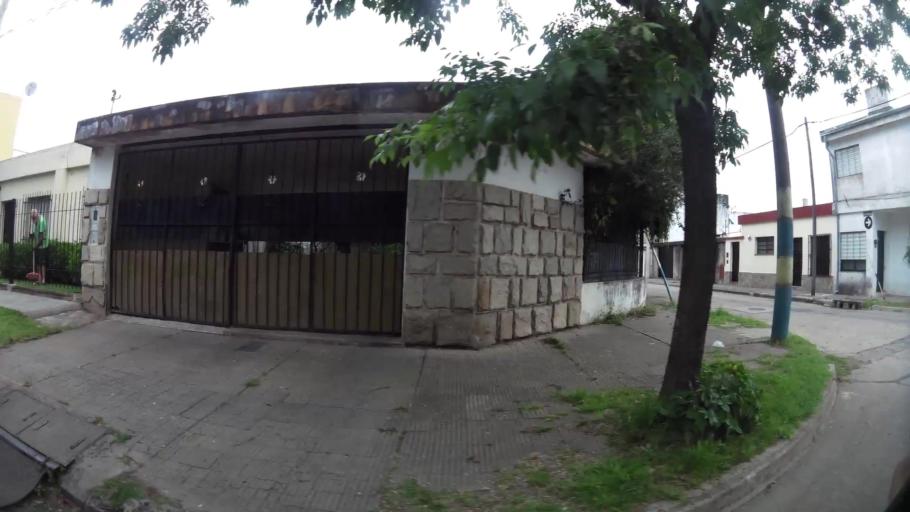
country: AR
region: Santa Fe
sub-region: Departamento de Rosario
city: Rosario
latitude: -32.9132
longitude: -60.6901
